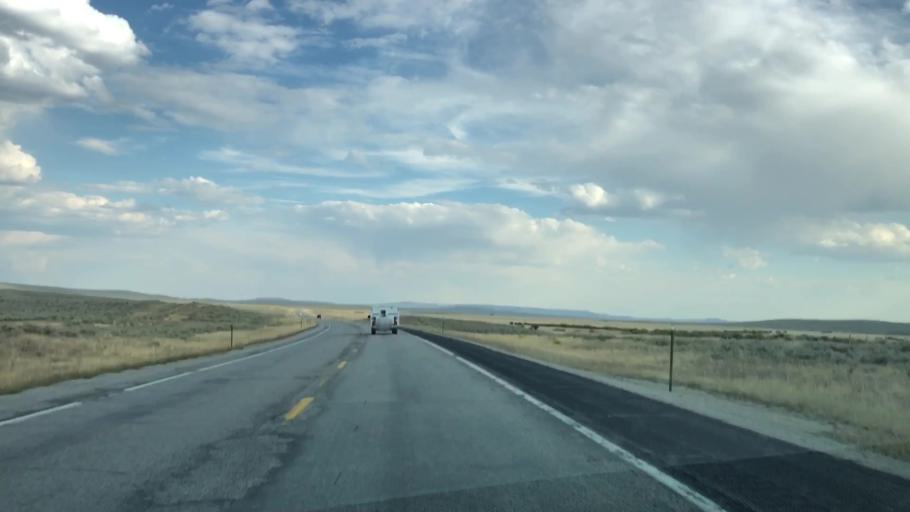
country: US
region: Wyoming
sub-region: Sublette County
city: Pinedale
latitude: 43.0473
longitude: -110.1483
